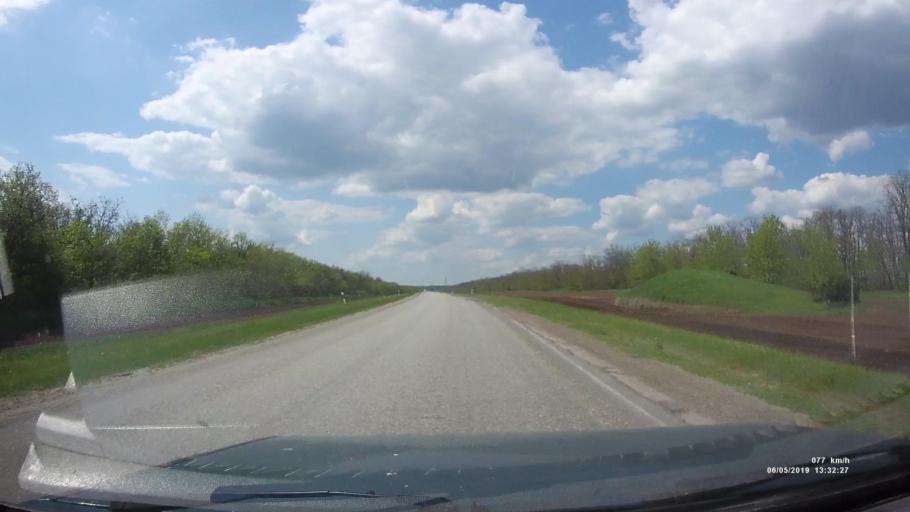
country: RU
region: Rostov
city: Ust'-Donetskiy
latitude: 47.6838
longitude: 40.7951
